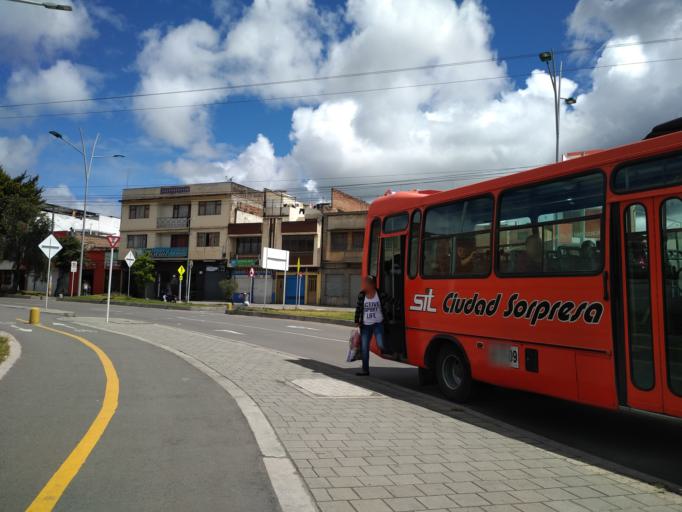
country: CO
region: Narino
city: Pasto
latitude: 1.2100
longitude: -77.2734
